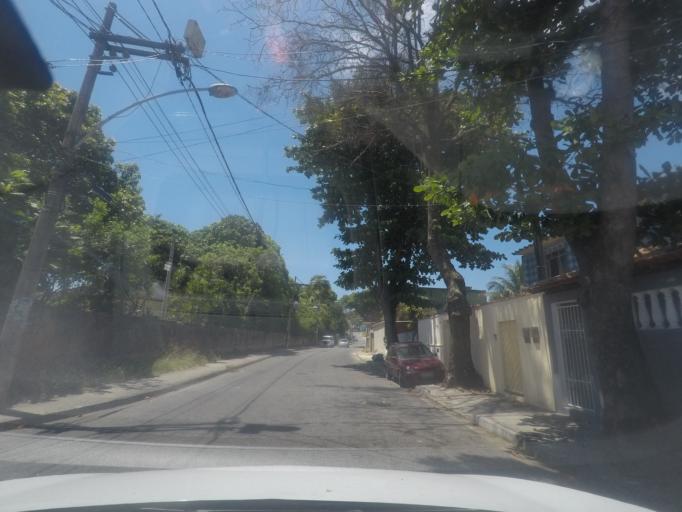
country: BR
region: Rio de Janeiro
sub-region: Itaguai
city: Itaguai
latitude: -22.9826
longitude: -43.6854
